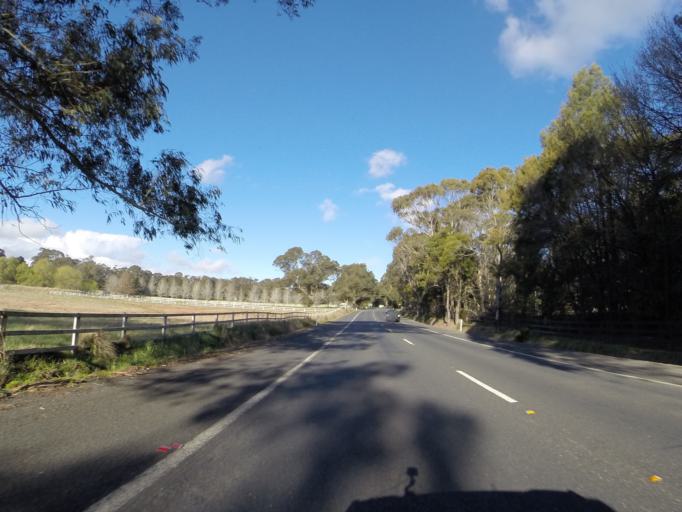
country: AU
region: New South Wales
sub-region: Wingecarribee
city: Bowral
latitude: -34.5800
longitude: 150.4987
